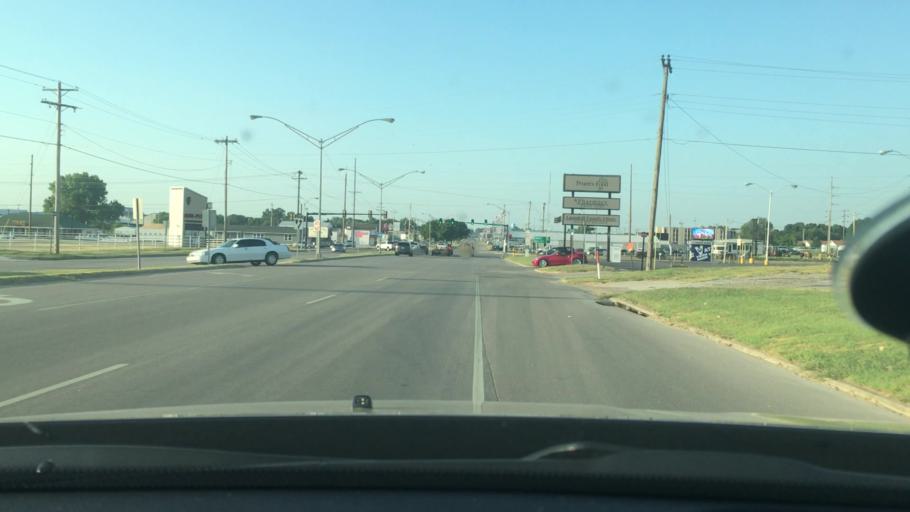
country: US
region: Oklahoma
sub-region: Pontotoc County
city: Ada
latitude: 34.7914
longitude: -96.6789
